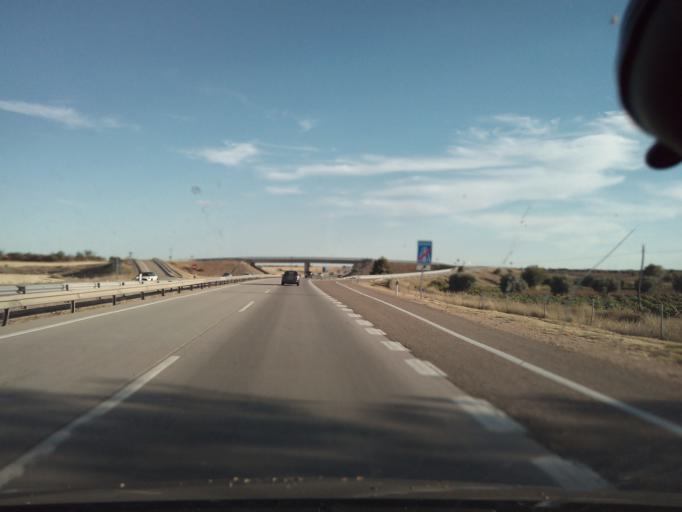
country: ES
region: Castille-La Mancha
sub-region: Province of Toledo
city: Dosbarrios
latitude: 39.8508
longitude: -3.4721
